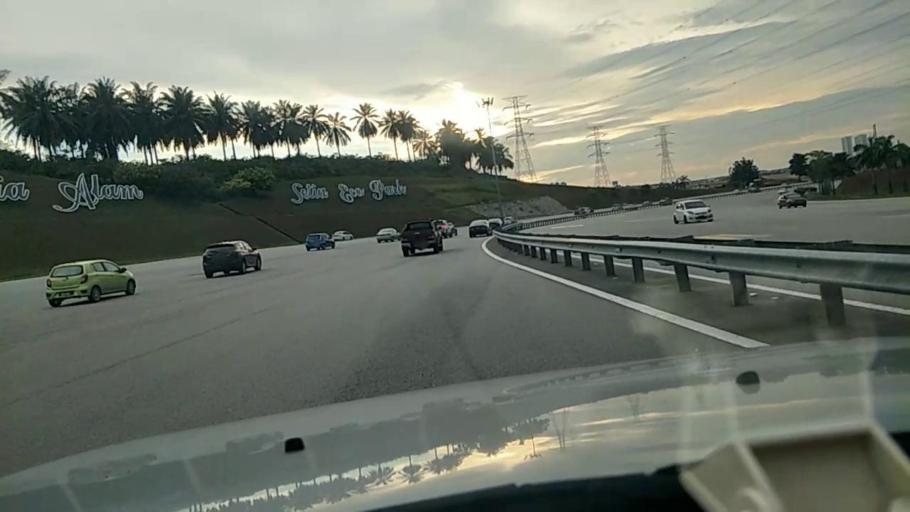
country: MY
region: Selangor
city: Shah Alam
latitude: 3.0918
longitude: 101.4848
